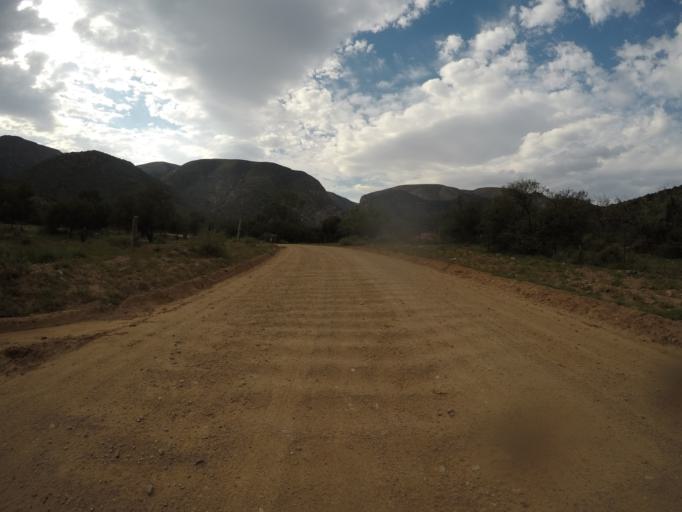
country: ZA
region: Eastern Cape
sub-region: Cacadu District Municipality
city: Kareedouw
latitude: -33.5842
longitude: 24.1657
